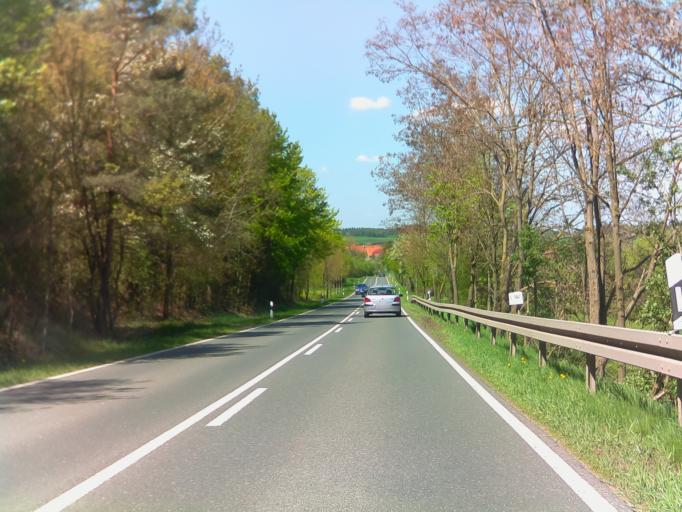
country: DE
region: Thuringia
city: Behringen
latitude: 50.7912
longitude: 10.9868
